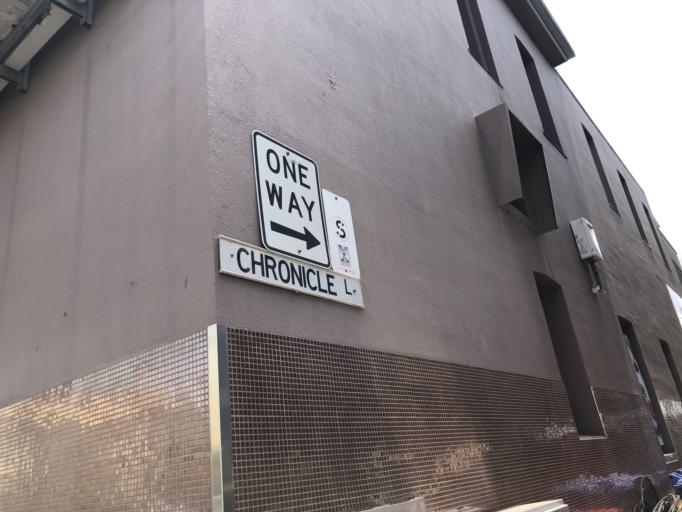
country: AU
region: Queensland
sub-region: Toowoomba
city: Toowoomba
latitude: -27.5609
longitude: 151.9555
